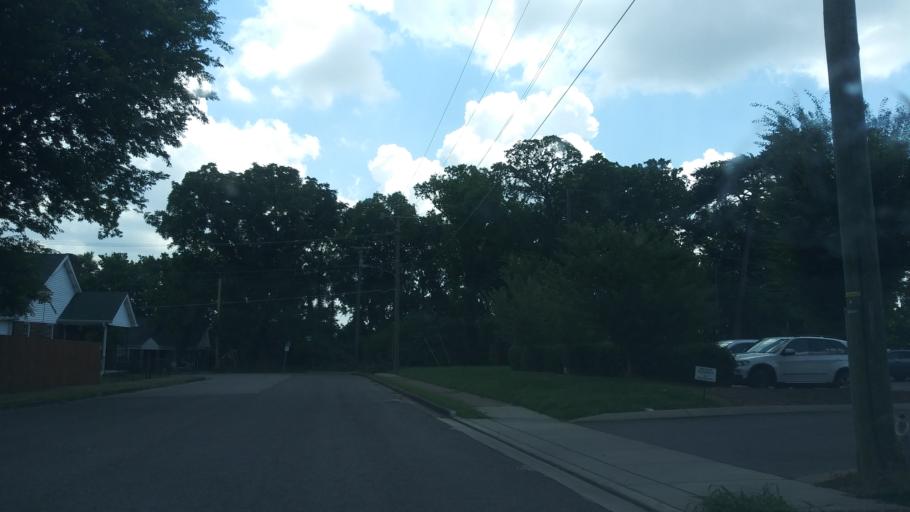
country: US
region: Tennessee
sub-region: Davidson County
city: Nashville
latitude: 36.1282
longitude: -86.7743
